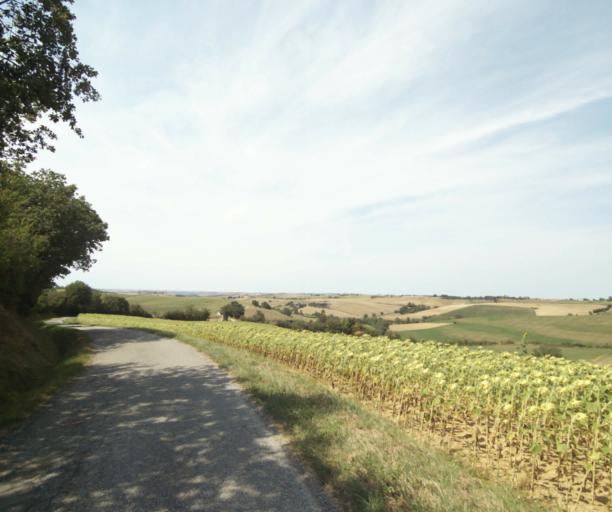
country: FR
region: Midi-Pyrenees
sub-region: Departement de la Haute-Garonne
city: Gaillac-Toulza
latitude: 43.2507
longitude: 1.4072
